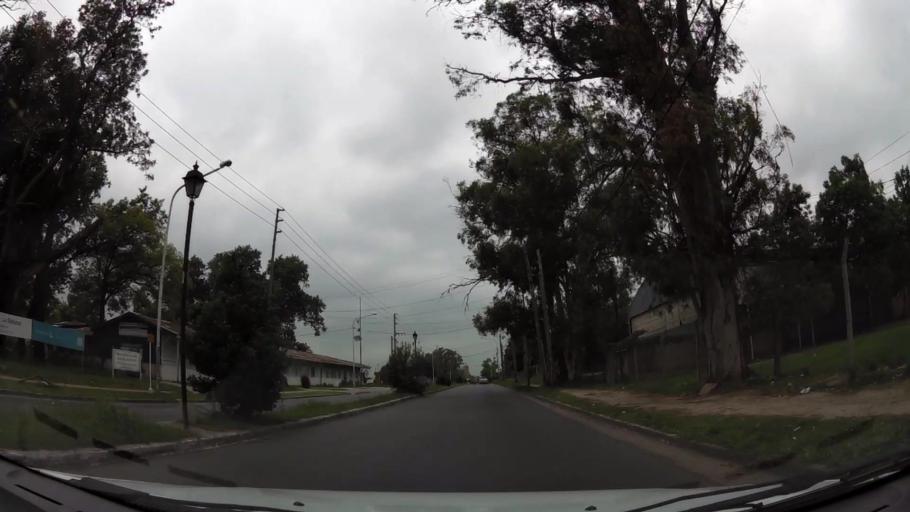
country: AR
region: Buenos Aires
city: San Justo
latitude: -34.7301
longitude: -58.5258
